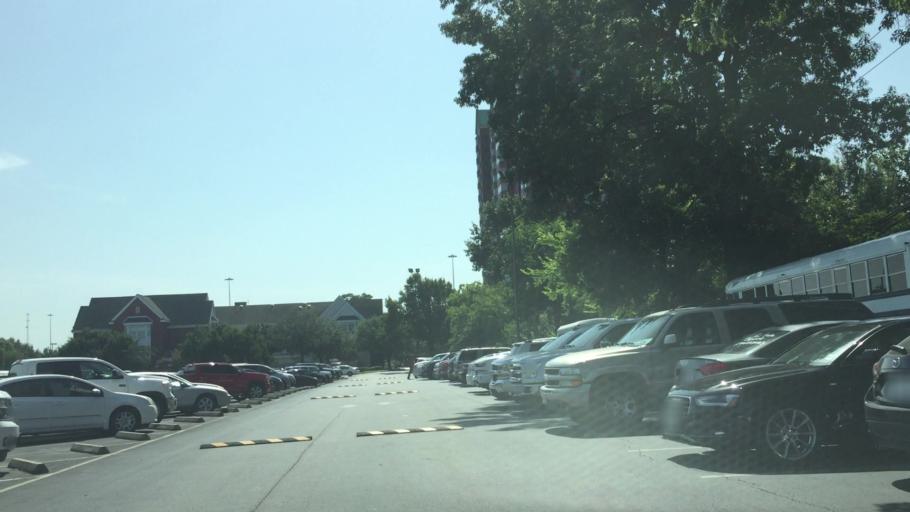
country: US
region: Texas
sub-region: Harris County
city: Hunters Creek Village
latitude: 29.7808
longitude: -95.4598
